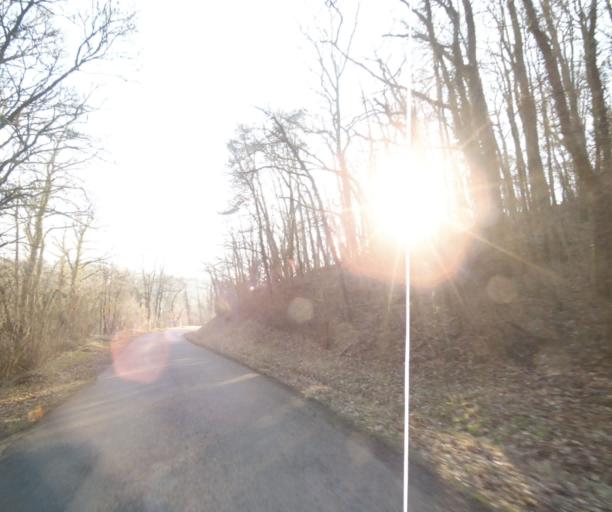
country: FR
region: Champagne-Ardenne
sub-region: Departement de la Haute-Marne
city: Chevillon
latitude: 48.5461
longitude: 5.1234
